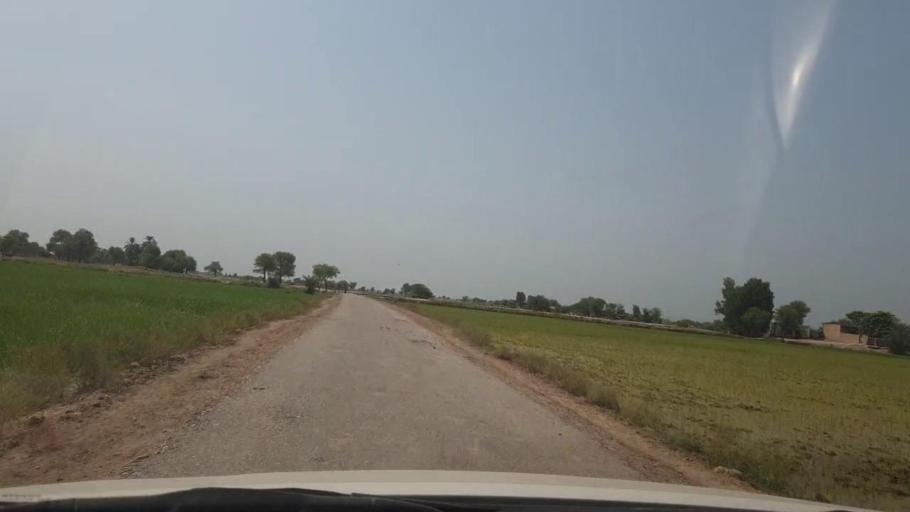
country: PK
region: Sindh
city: Shikarpur
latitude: 28.0056
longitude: 68.7140
